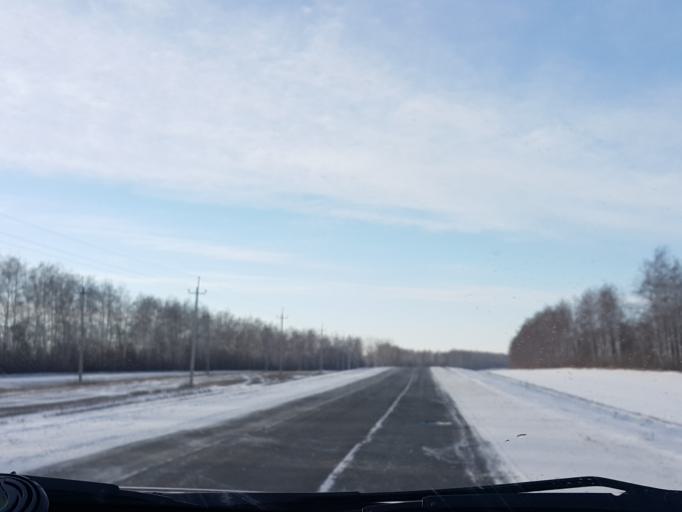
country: RU
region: Tambov
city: Znamenka
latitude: 52.3846
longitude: 41.3357
